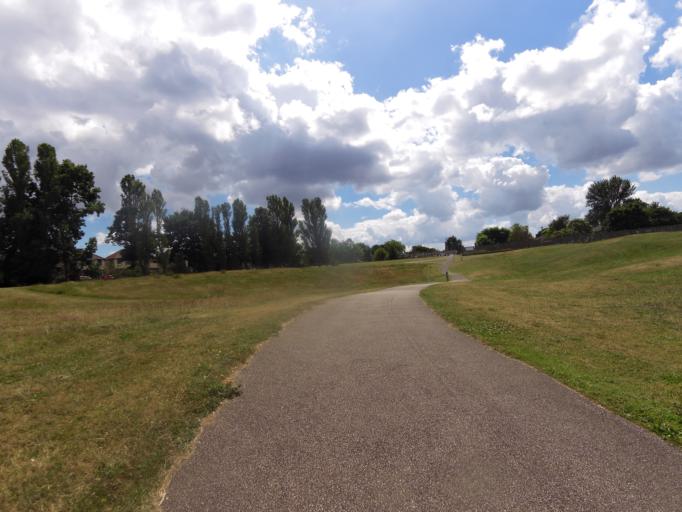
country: GB
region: England
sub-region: Suffolk
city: Ipswich
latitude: 52.0392
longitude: 1.1791
